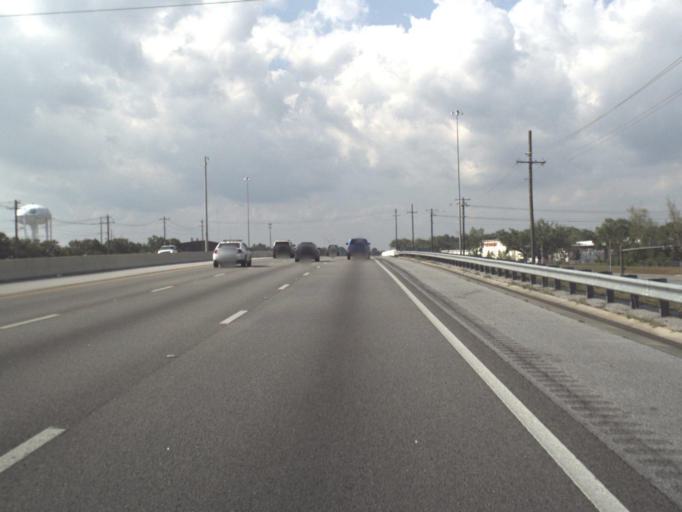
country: US
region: Florida
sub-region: Escambia County
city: Brent
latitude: 30.4708
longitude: -87.2278
